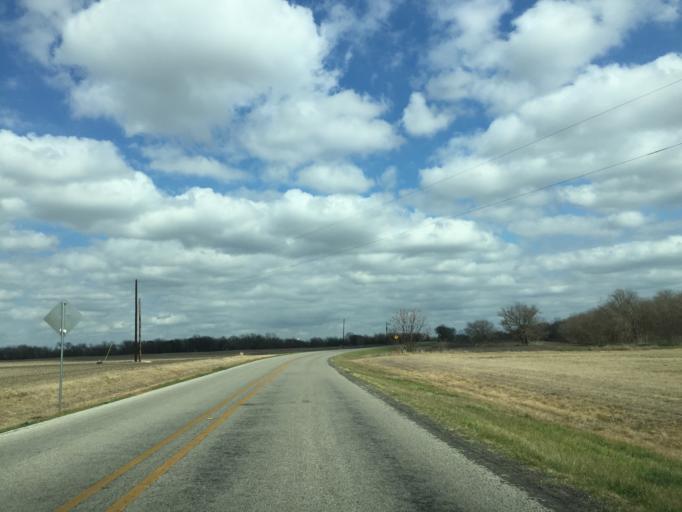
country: US
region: Texas
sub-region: Williamson County
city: Granger
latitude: 30.7072
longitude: -97.4656
